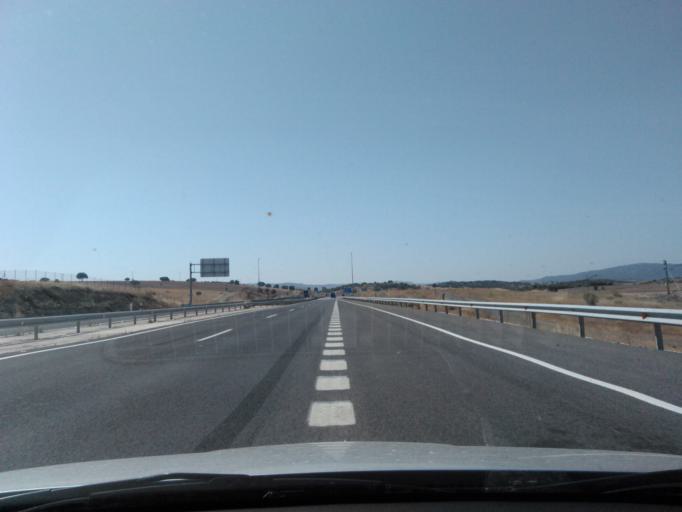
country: ES
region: Castille-La Mancha
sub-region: Provincia de Ciudad Real
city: Viso del Marques
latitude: 38.4914
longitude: -3.5025
